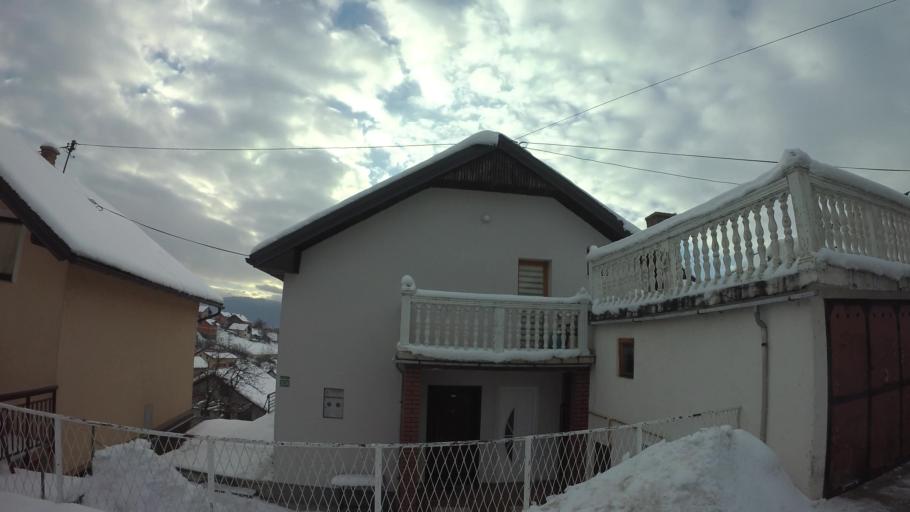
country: BA
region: Federation of Bosnia and Herzegovina
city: Kobilja Glava
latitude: 43.8607
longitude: 18.3773
